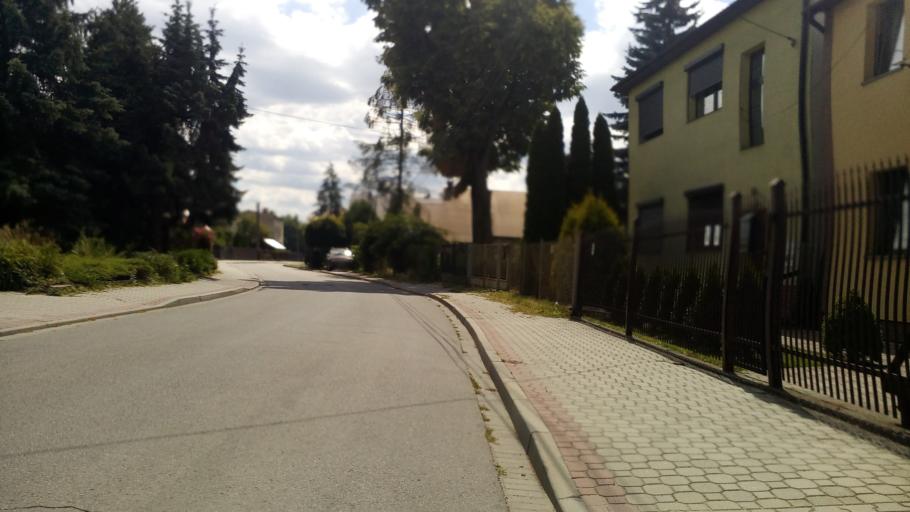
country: PL
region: Lesser Poland Voivodeship
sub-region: Powiat nowosadecki
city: Nowy Sacz
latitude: 49.6140
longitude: 20.6846
